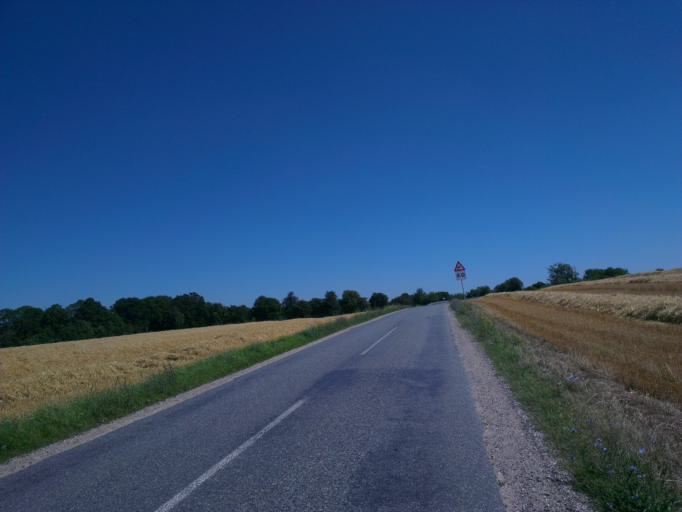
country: DK
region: Capital Region
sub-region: Egedal Kommune
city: Olstykke
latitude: 55.8335
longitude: 12.1345
